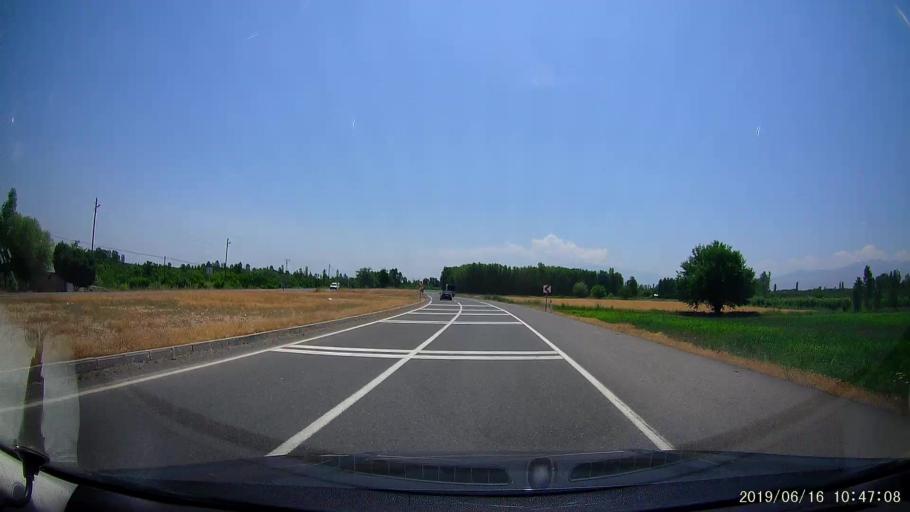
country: AM
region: Armavir
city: Shenavan
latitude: 40.0147
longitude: 43.8852
